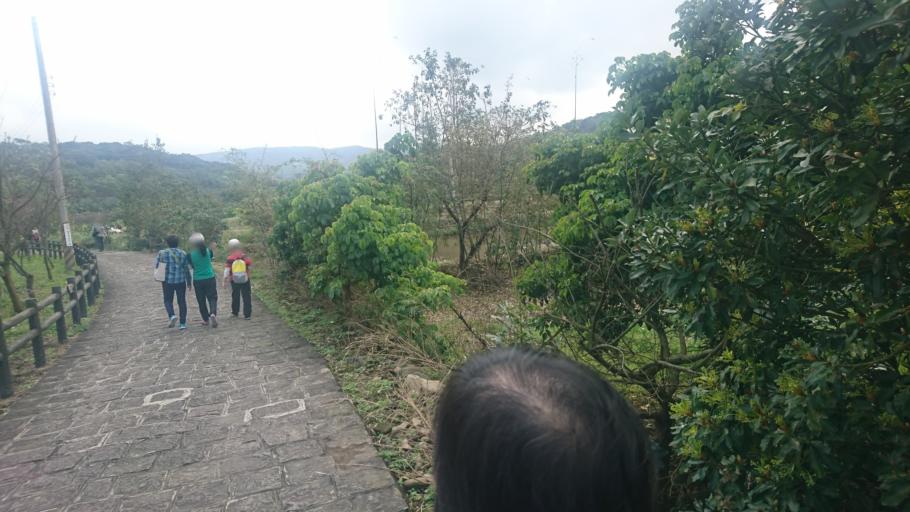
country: TW
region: Taipei
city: Taipei
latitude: 25.2648
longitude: 121.5138
